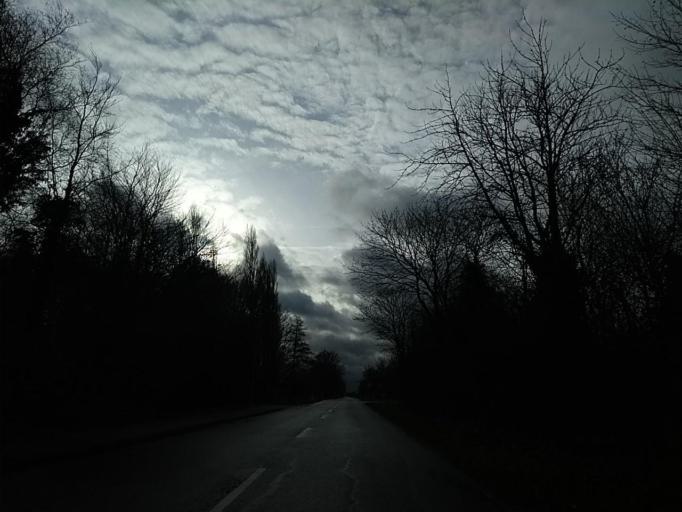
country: DE
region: Lower Saxony
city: Emden
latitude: 53.3170
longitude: 7.2552
